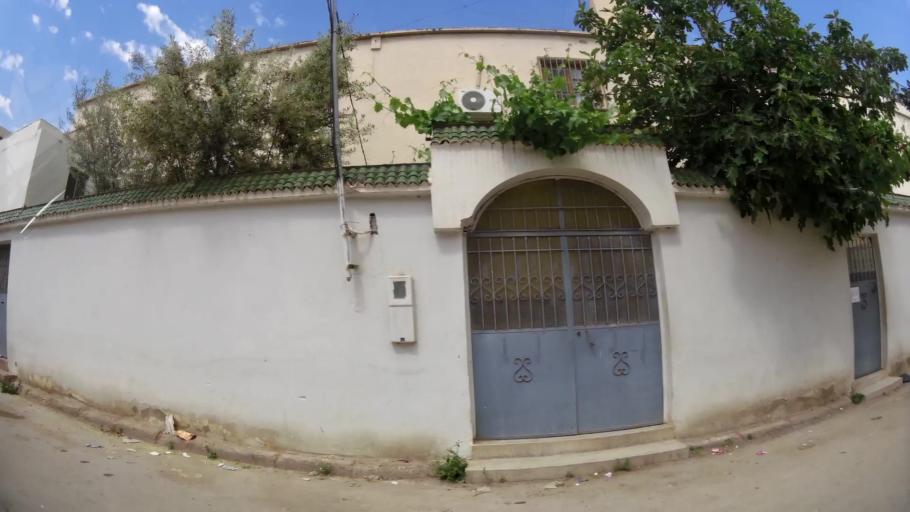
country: MA
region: Oriental
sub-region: Oujda-Angad
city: Oujda
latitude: 34.6830
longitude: -1.9031
